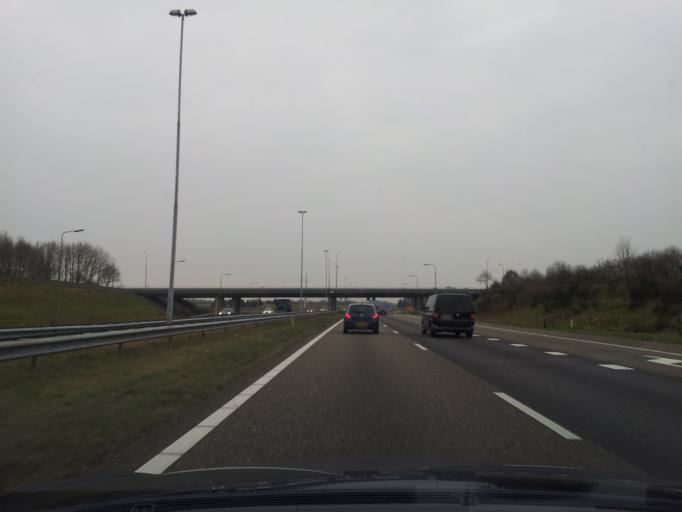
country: NL
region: North Brabant
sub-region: Gemeente Breda
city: Breda
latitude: 51.5385
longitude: 4.8013
